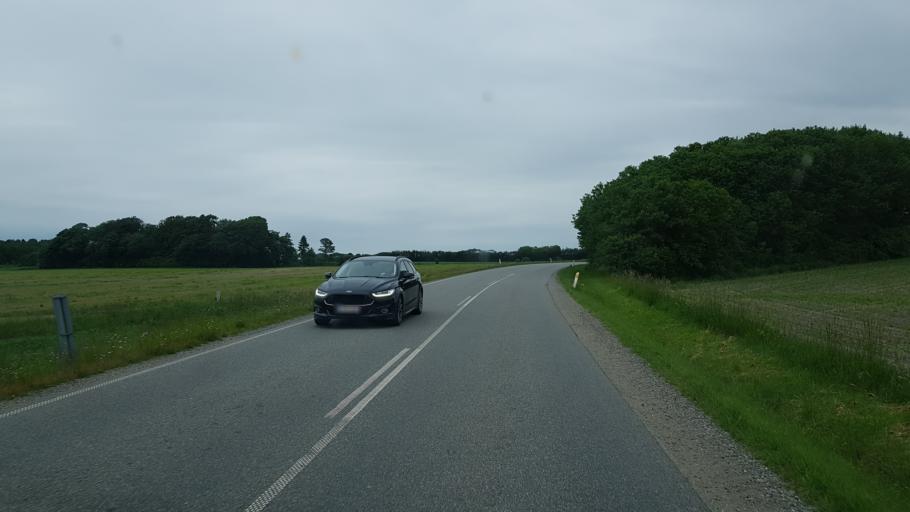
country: DK
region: South Denmark
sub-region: Varde Kommune
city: Olgod
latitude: 55.7140
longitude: 8.6999
